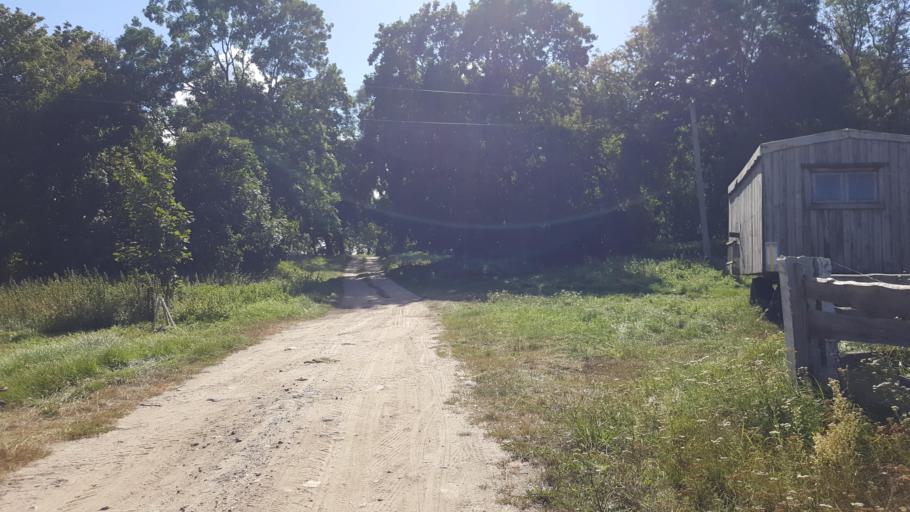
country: BY
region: Brest
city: Vysokaye
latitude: 52.2743
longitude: 23.5003
